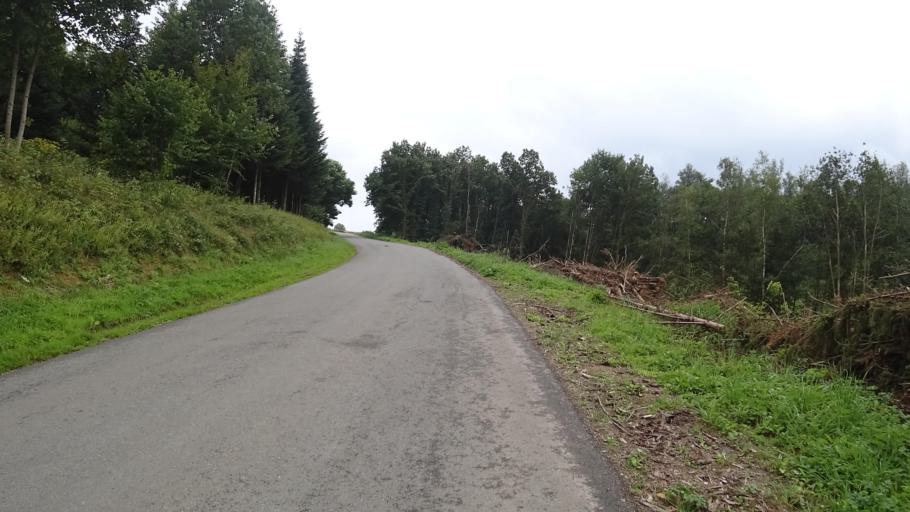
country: BE
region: Wallonia
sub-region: Province du Luxembourg
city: Chiny
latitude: 49.8011
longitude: 5.3732
